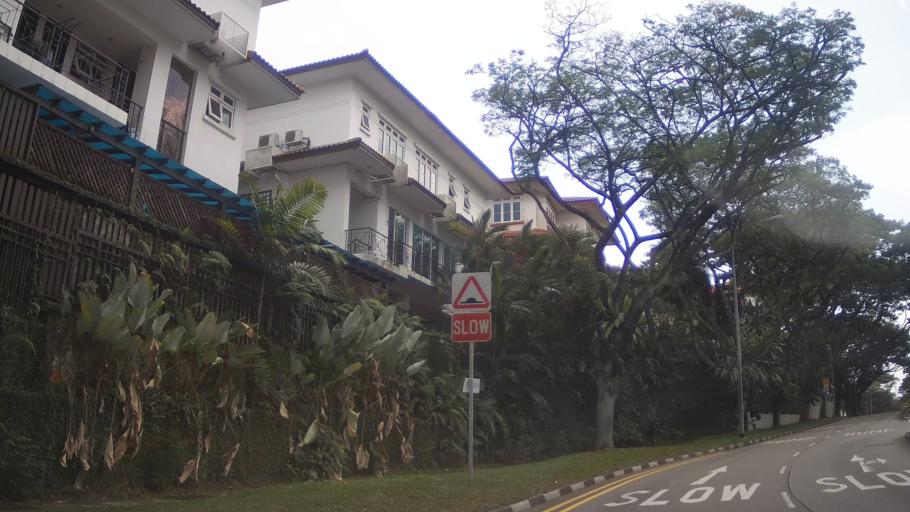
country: MY
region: Johor
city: Johor Bahru
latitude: 1.3738
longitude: 103.7715
